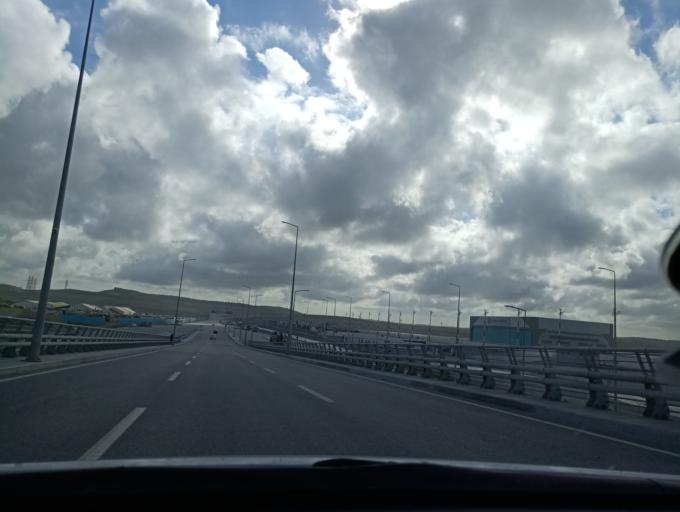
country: TR
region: Istanbul
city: Durusu
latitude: 41.2570
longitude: 28.7389
